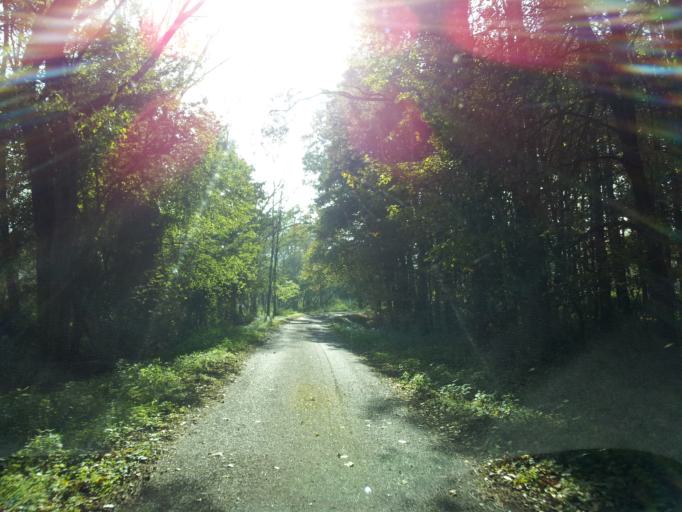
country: HU
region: Gyor-Moson-Sopron
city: Bakonyszentlaszlo
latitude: 47.3652
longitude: 17.8190
